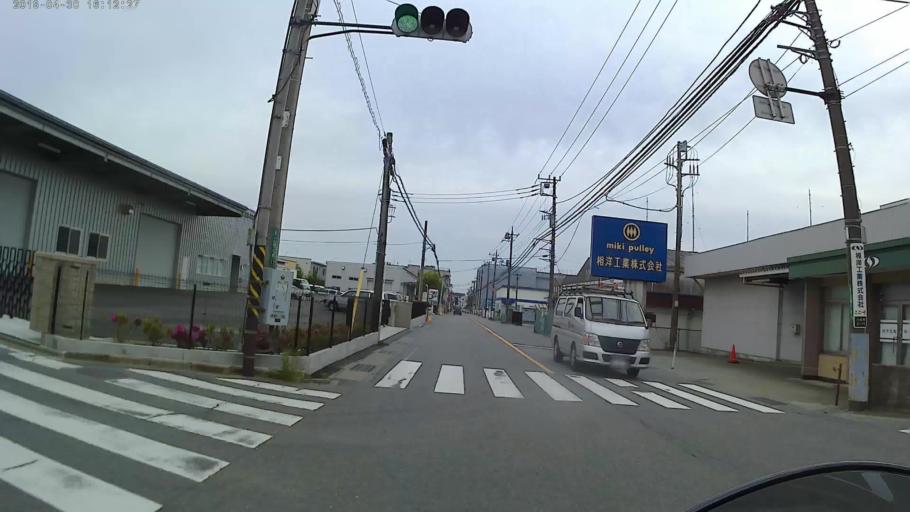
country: JP
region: Kanagawa
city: Minami-rinkan
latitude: 35.4960
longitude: 139.4293
